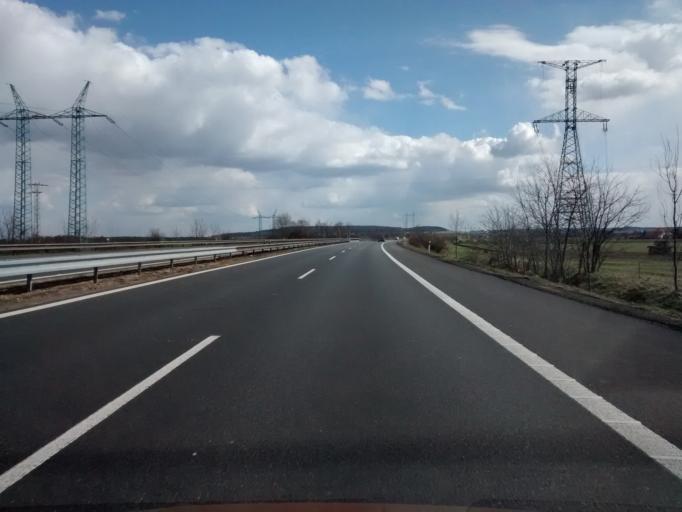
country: CZ
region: Central Bohemia
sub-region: Okres Melnik
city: Veltrusy
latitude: 50.2982
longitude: 14.3407
